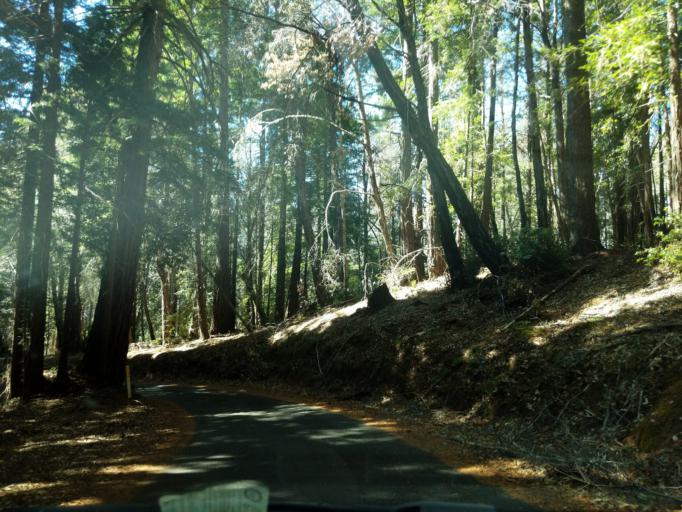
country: US
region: California
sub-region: Sonoma County
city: Monte Rio
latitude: 38.5254
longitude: -123.2297
